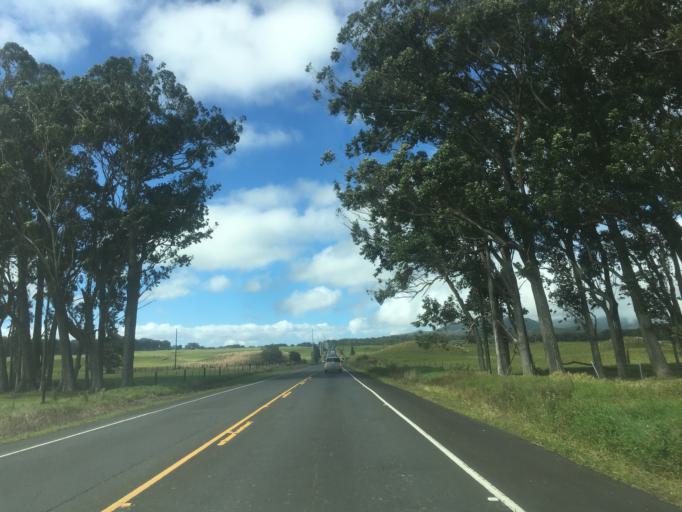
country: US
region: Hawaii
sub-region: Hawaii County
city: Waimea
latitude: 20.0493
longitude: -155.5721
